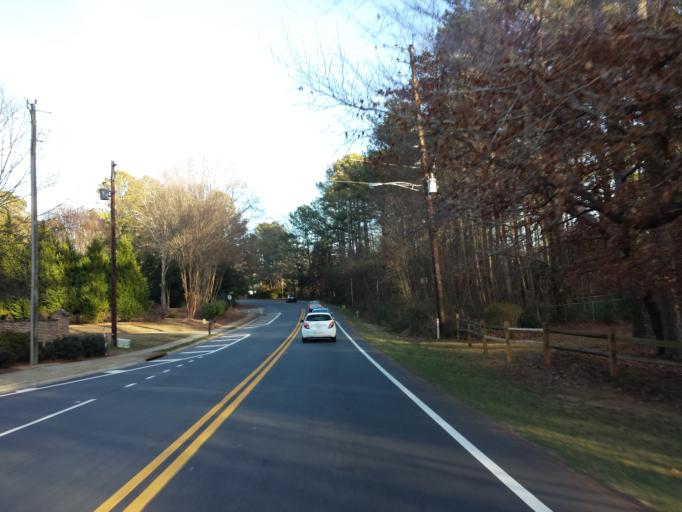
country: US
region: Georgia
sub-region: Fulton County
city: Roswell
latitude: 33.9936
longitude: -84.4423
